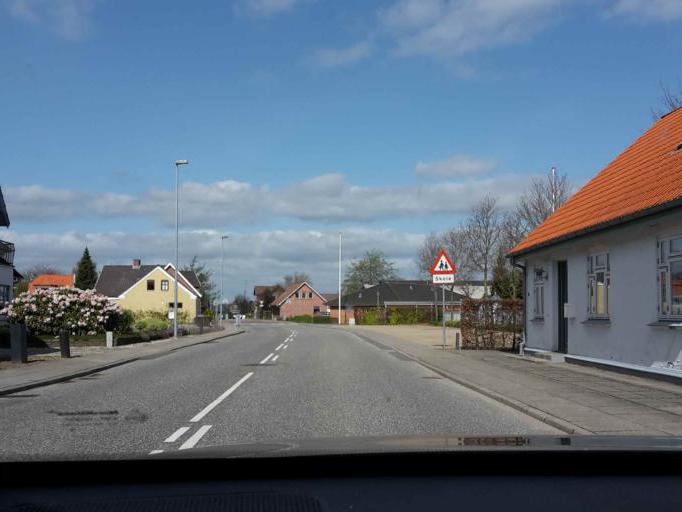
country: DK
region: South Denmark
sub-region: Billund Kommune
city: Grindsted
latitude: 55.6944
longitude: 8.8416
